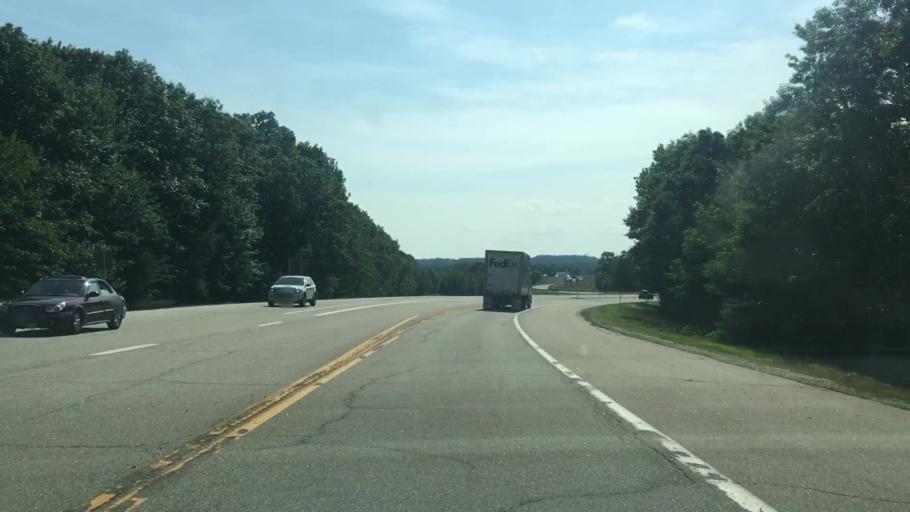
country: US
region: New Hampshire
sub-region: Strafford County
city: Rochester
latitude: 43.3275
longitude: -70.9811
